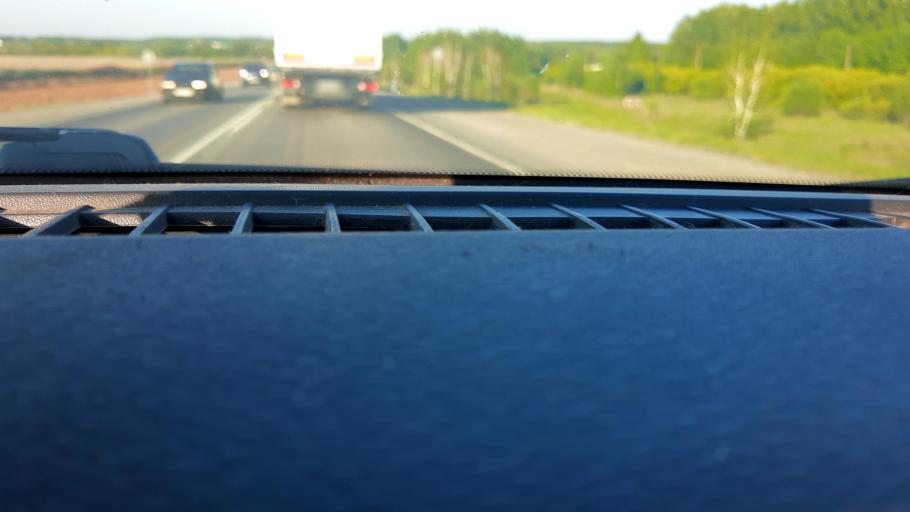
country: RU
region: Bashkortostan
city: Iglino
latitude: 54.7276
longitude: 56.2557
